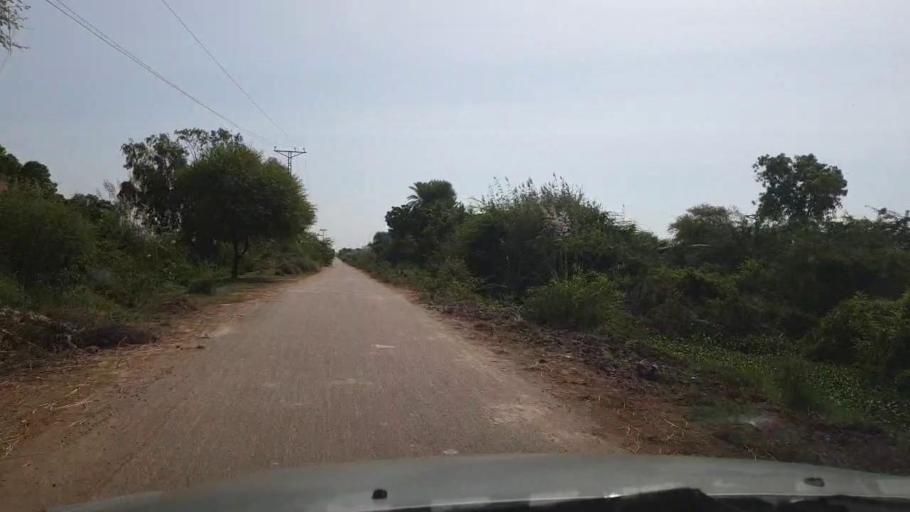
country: PK
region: Sindh
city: Tando Muhammad Khan
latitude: 25.1536
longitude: 68.3842
